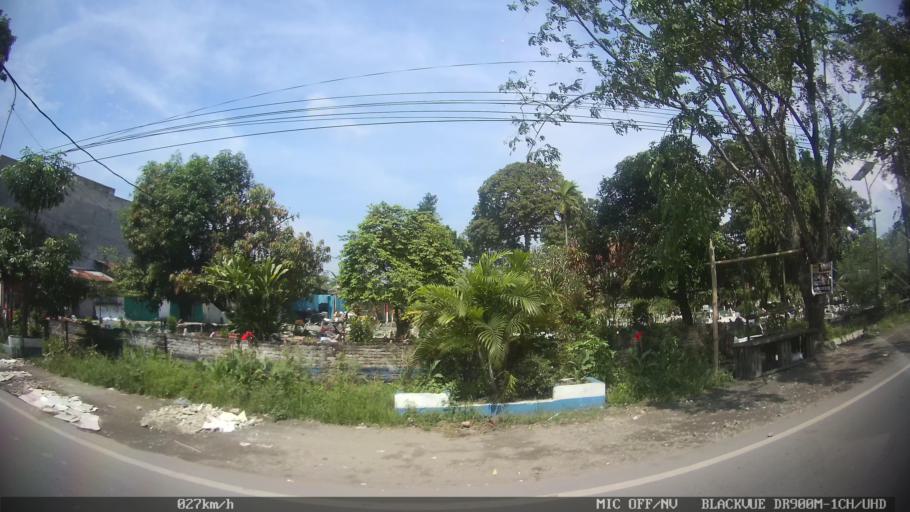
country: ID
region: North Sumatra
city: Medan
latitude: 3.6379
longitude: 98.6583
